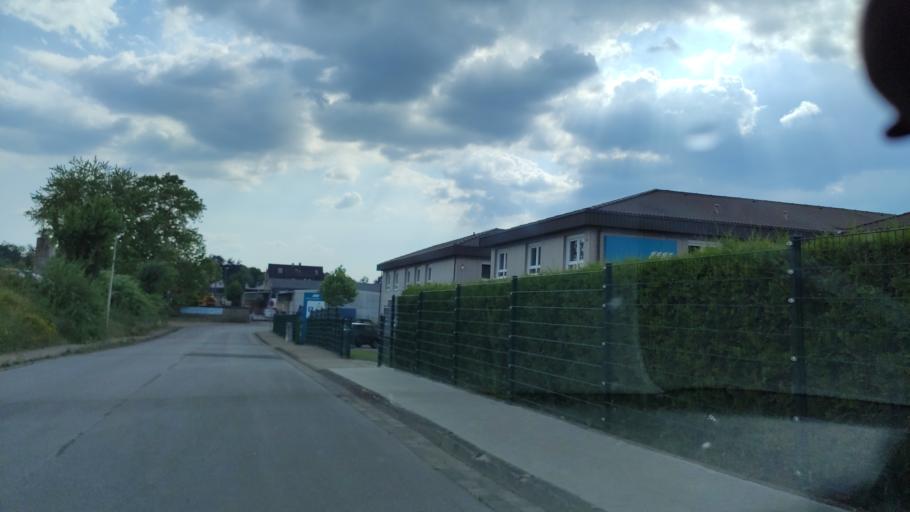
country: DE
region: Lower Saxony
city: Holzminden
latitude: 51.8391
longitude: 9.4651
